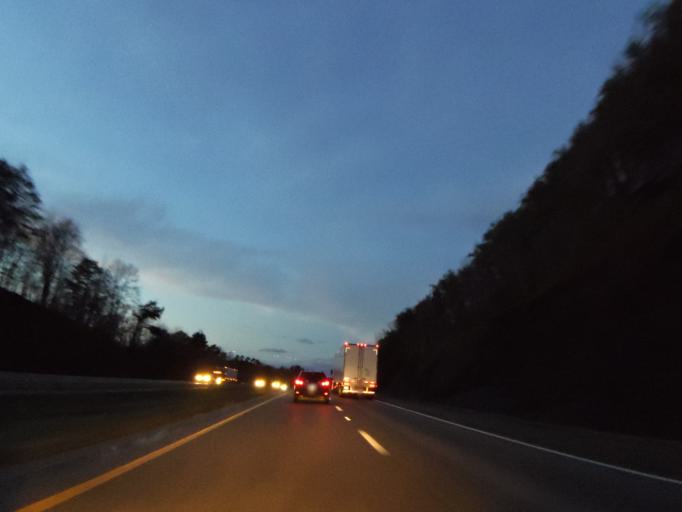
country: US
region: Kentucky
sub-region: Whitley County
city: Corbin
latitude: 36.8769
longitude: -84.1495
